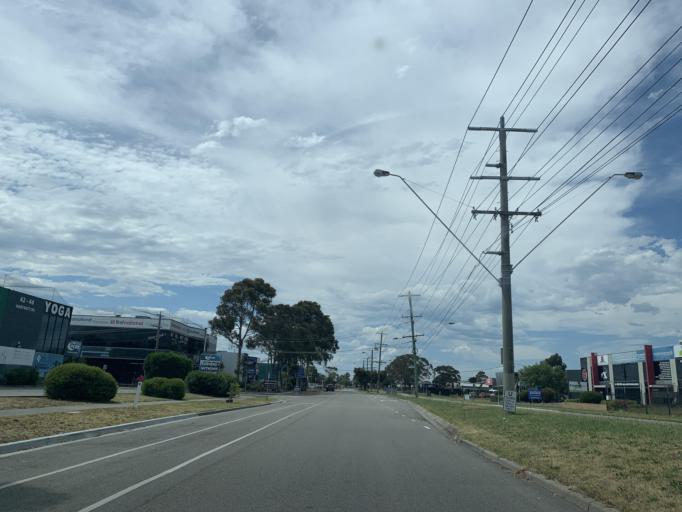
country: AU
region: Victoria
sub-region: Frankston
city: Frankston North
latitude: -38.1157
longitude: 145.1409
